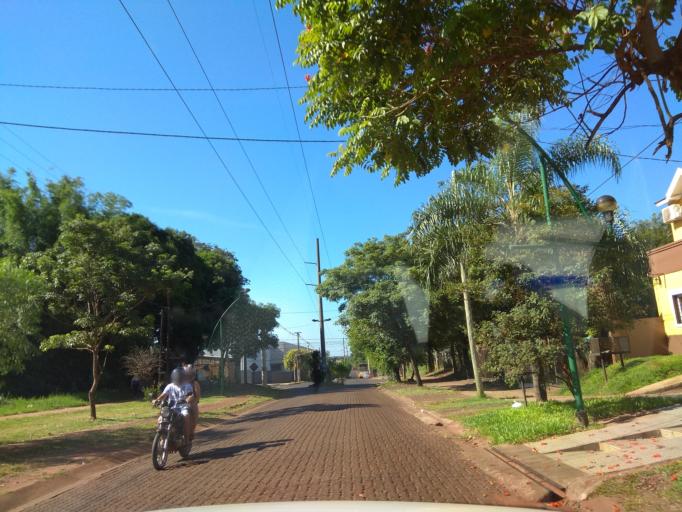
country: AR
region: Misiones
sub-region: Departamento de Capital
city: Posadas
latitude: -27.3985
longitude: -55.9171
